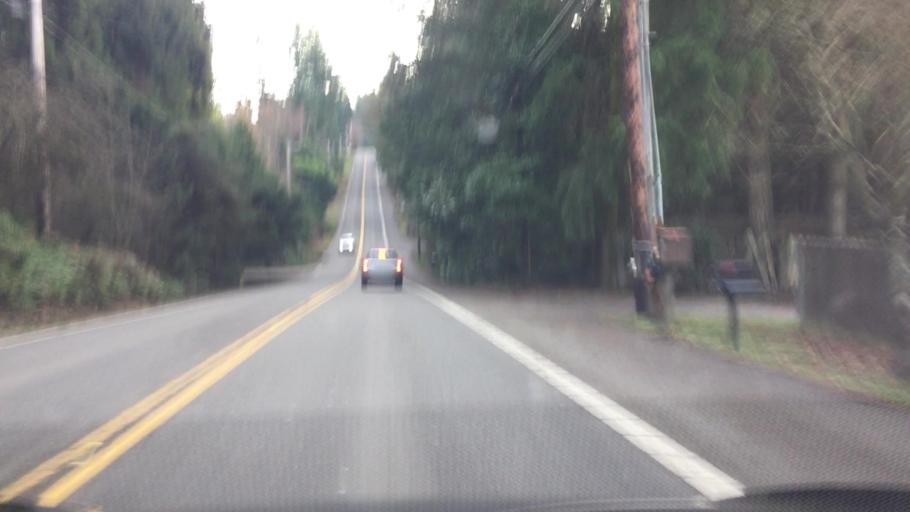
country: US
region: Washington
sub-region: King County
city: Woodinville
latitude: 47.7667
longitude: -122.1317
